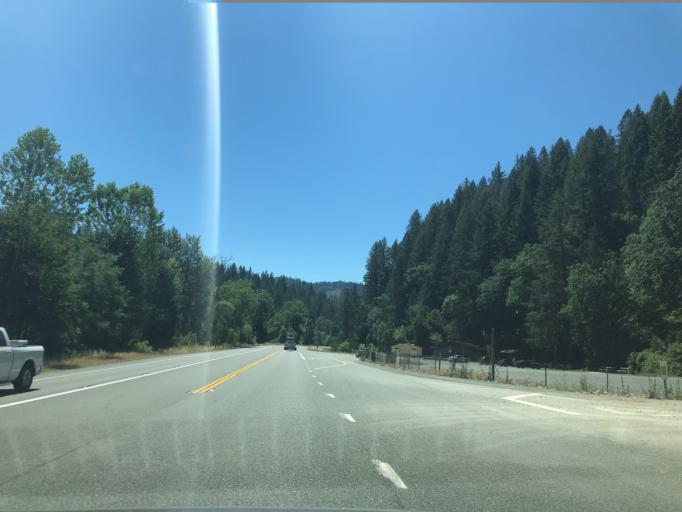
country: US
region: California
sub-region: Trinity County
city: Weaverville
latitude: 40.6673
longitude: -122.9437
